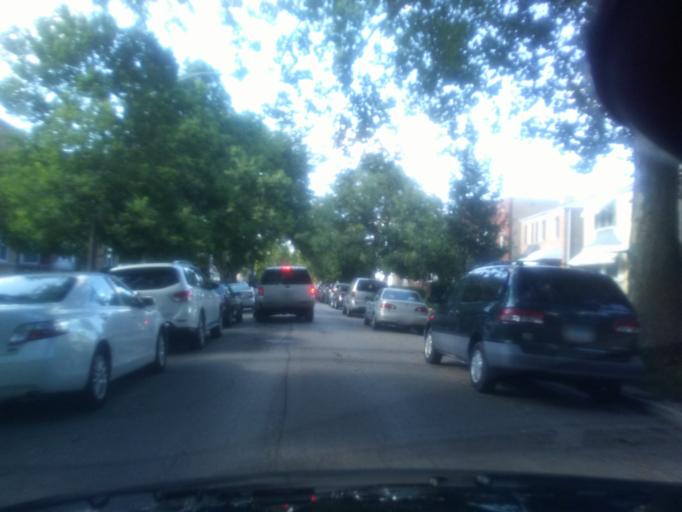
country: US
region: Illinois
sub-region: Cook County
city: Lincolnwood
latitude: 41.9742
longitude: -87.7184
